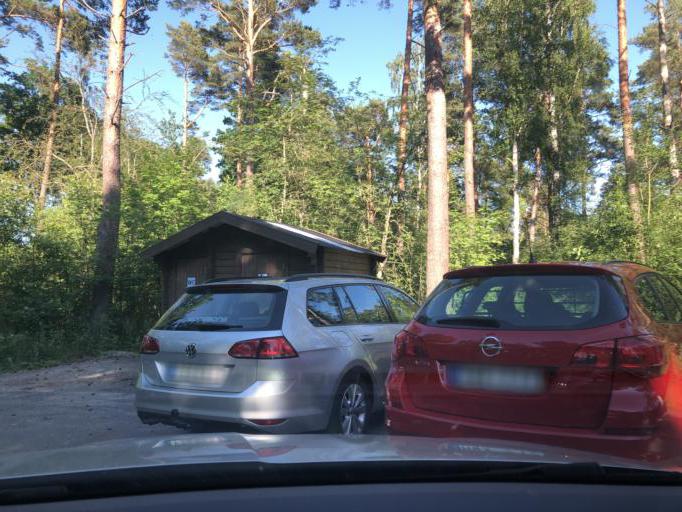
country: SE
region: Blekinge
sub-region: Karlshamns Kommun
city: Morrum
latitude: 56.1522
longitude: 14.7988
